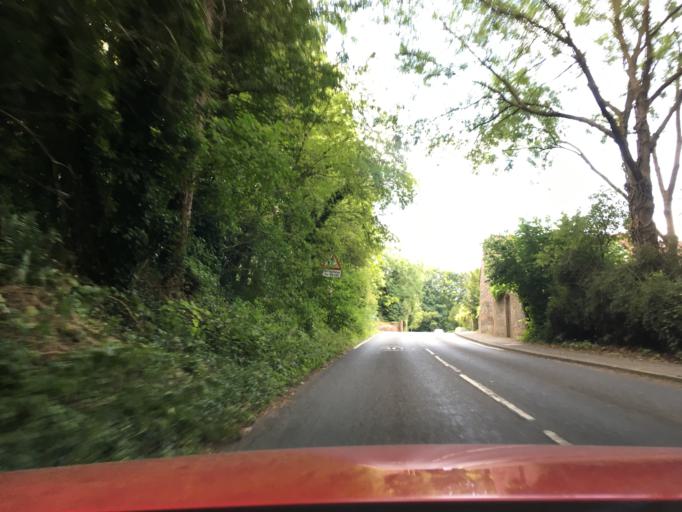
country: GB
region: England
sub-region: Hampshire
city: Kings Worthy
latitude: 51.0873
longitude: -1.3052
